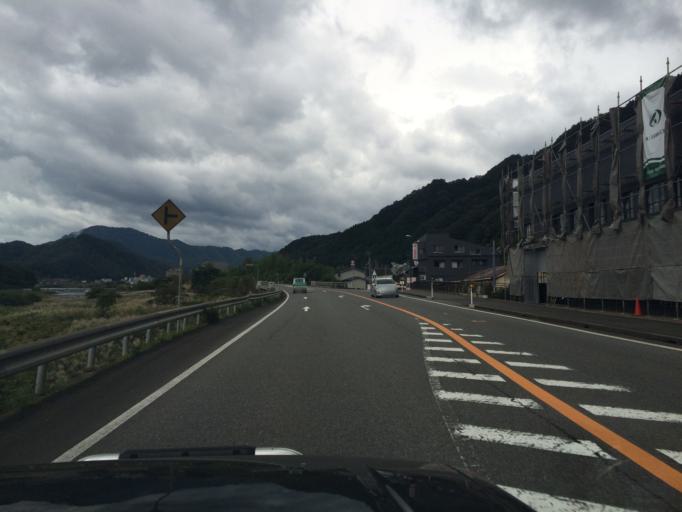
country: JP
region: Hyogo
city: Toyooka
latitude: 35.4177
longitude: 134.7859
